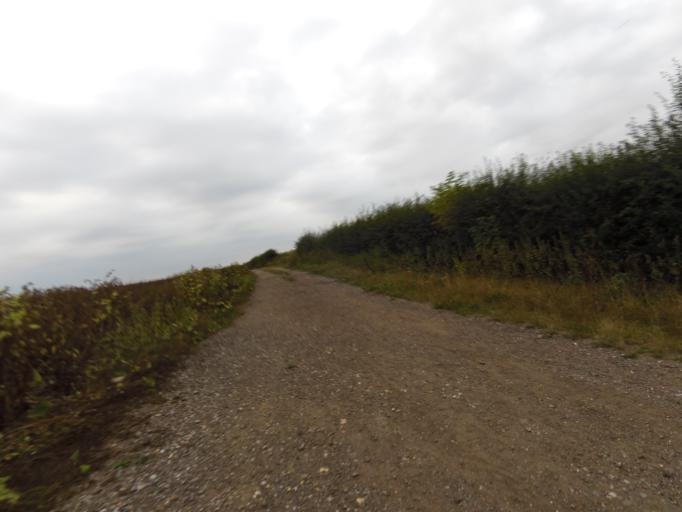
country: GB
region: England
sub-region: Hertfordshire
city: Radlett
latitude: 51.7153
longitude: -0.3132
